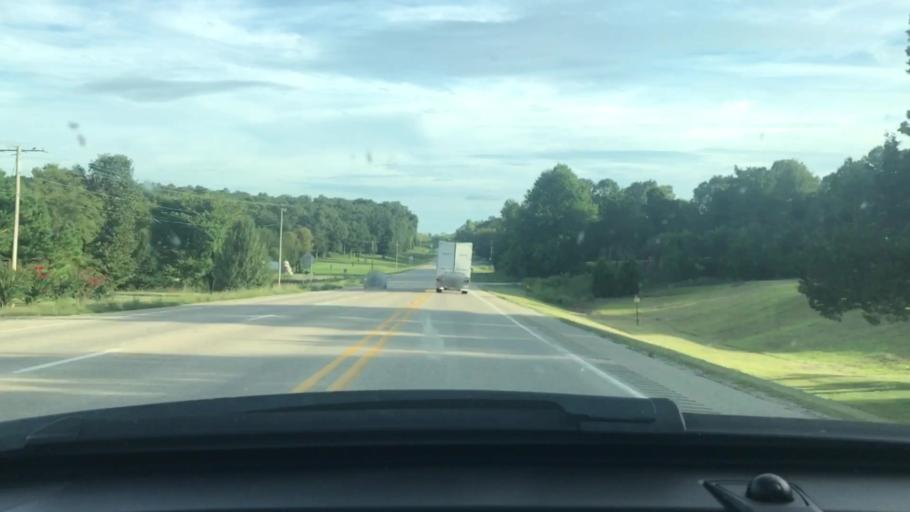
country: US
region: Arkansas
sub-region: Lawrence County
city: Hoxie
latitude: 36.1544
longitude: -91.1615
